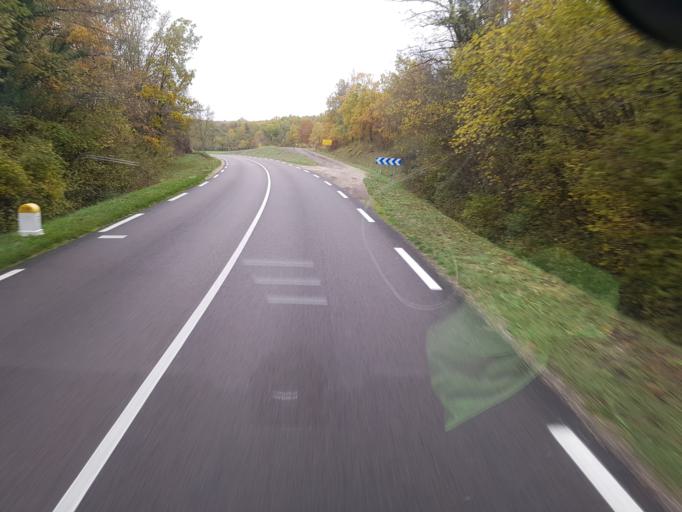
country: FR
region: Bourgogne
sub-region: Departement de la Cote-d'Or
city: Is-sur-Tille
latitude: 47.5232
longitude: 5.0012
